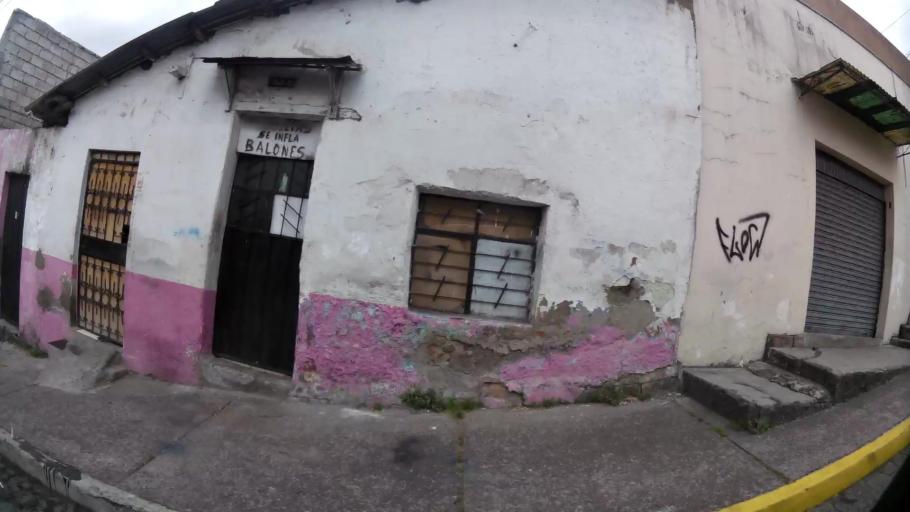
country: EC
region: Pichincha
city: Quito
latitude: -0.2118
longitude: -78.5107
